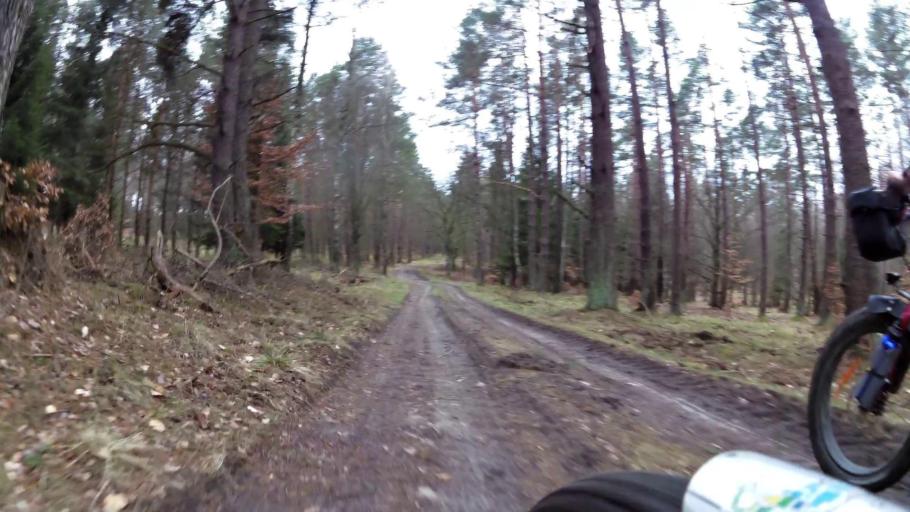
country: PL
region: Pomeranian Voivodeship
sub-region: Powiat bytowski
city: Trzebielino
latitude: 54.1349
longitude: 17.1440
